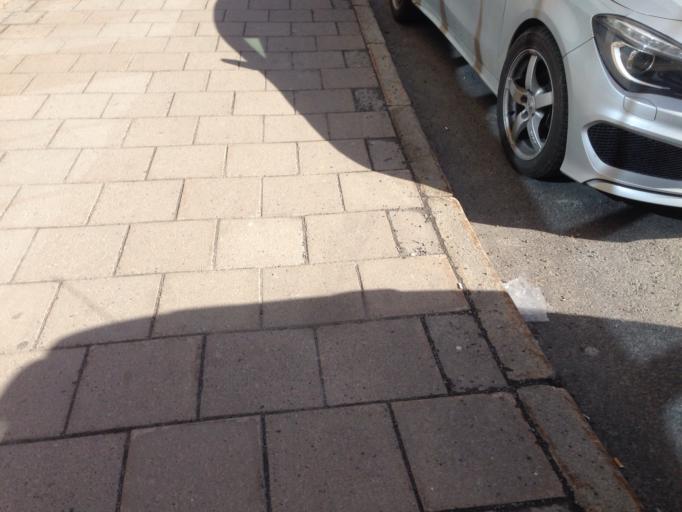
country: SE
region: Stockholm
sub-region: Stockholms Kommun
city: Stockholm
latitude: 59.3417
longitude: 18.0633
